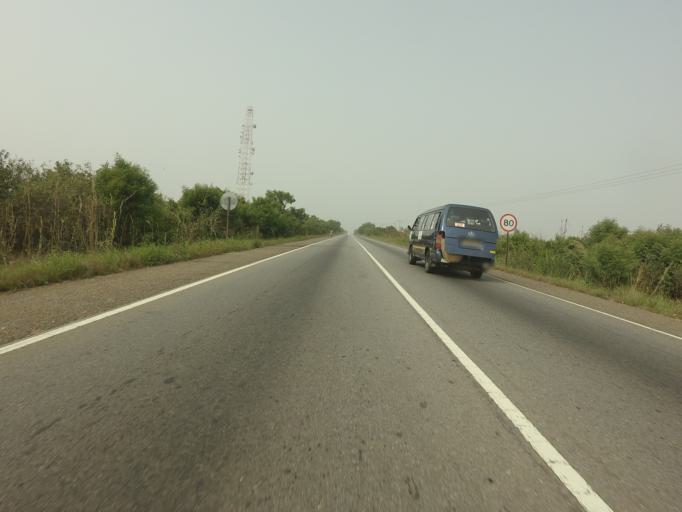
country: GH
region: Volta
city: Anloga
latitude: 5.9358
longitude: 0.5235
